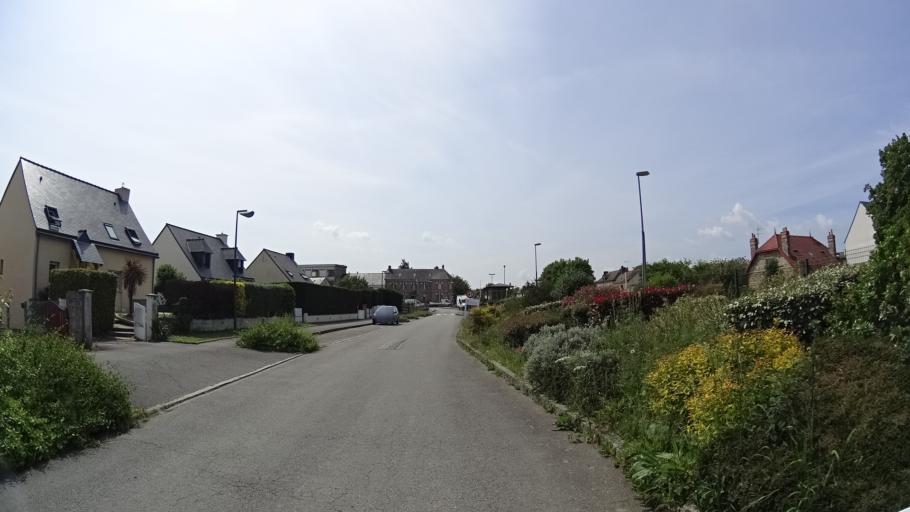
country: FR
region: Brittany
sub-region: Departement d'Ille-et-Vilaine
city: Saint-Armel
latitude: 48.0151
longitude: -1.5948
